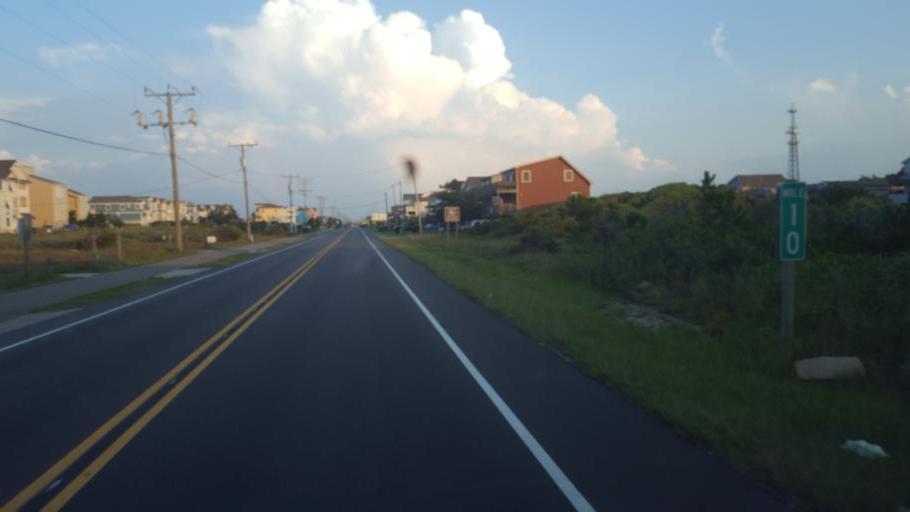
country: US
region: North Carolina
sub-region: Dare County
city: Nags Head
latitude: 35.9923
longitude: -75.6444
